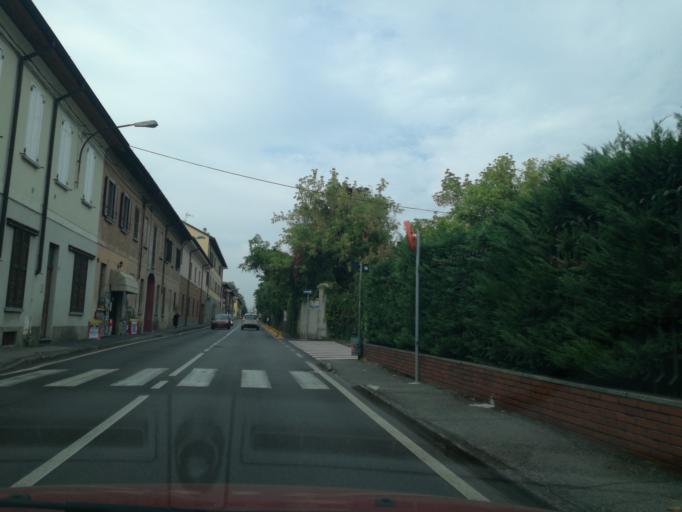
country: IT
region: Lombardy
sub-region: Provincia di Monza e Brianza
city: Vimercate
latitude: 45.6207
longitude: 9.3706
